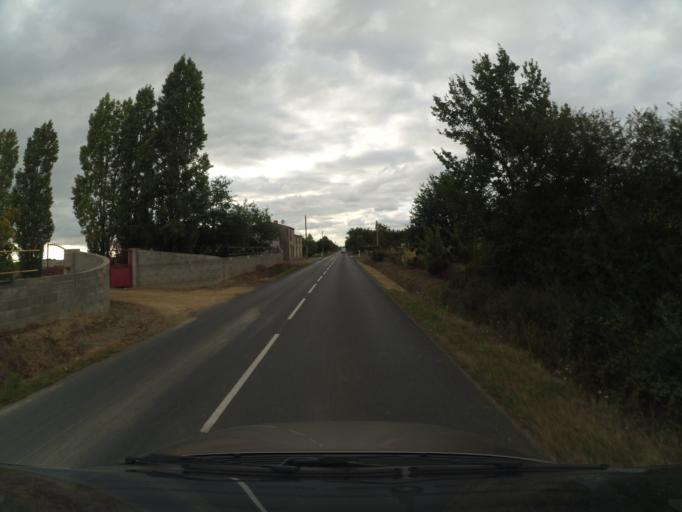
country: FR
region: Pays de la Loire
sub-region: Departement de la Vendee
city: Saint-Andre-Treize-Voies
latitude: 46.9178
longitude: -1.3880
